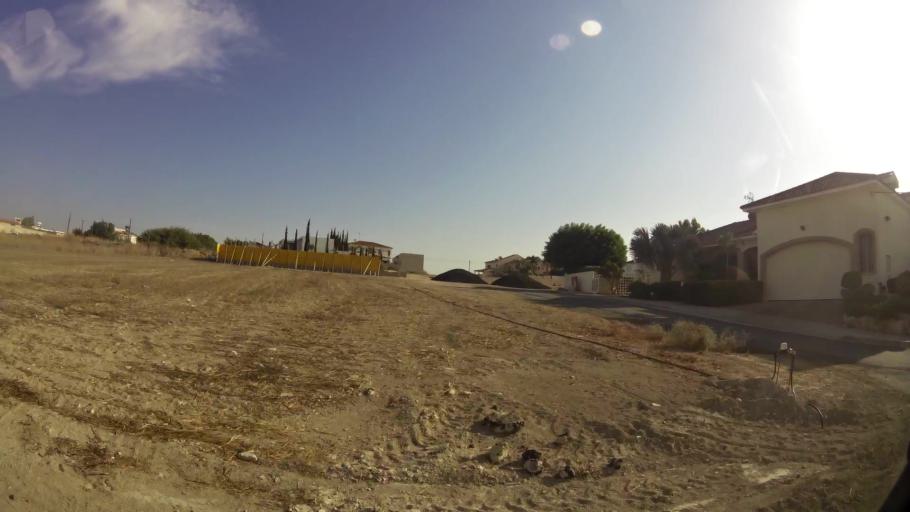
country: CY
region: Larnaka
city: Aradippou
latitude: 34.9497
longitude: 33.6012
